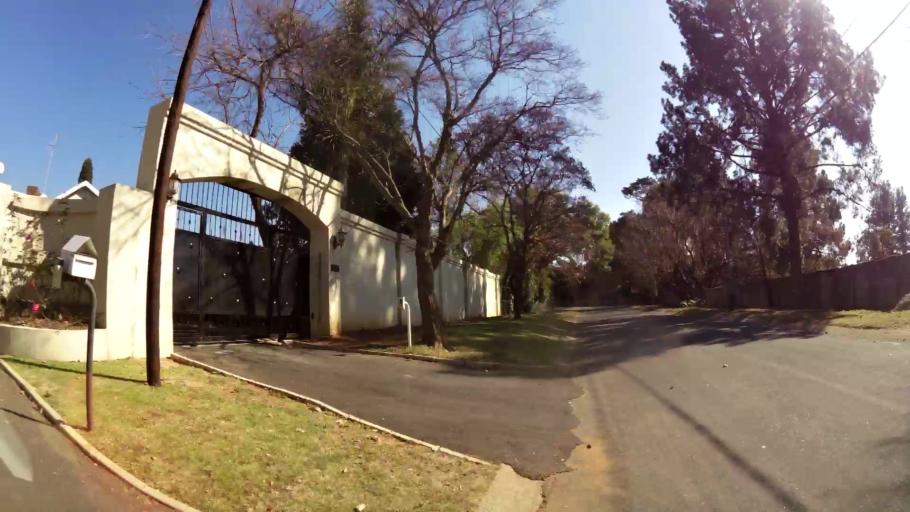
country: ZA
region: Gauteng
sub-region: City of Johannesburg Metropolitan Municipality
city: Modderfontein
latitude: -26.1356
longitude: 28.1156
